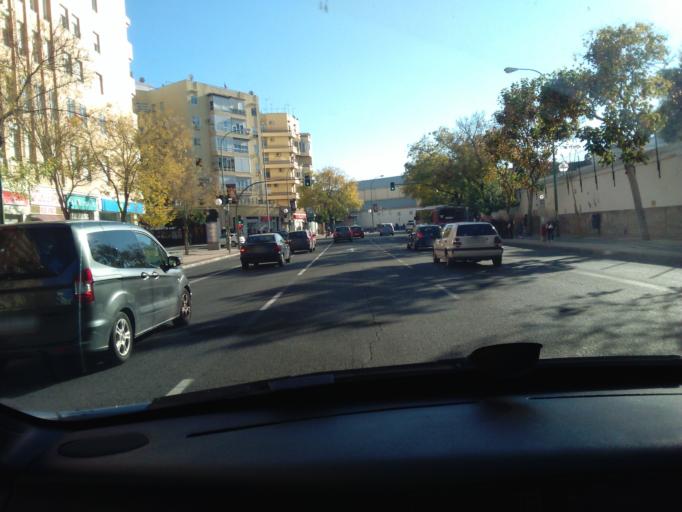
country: ES
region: Andalusia
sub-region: Provincia de Sevilla
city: Sevilla
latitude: 37.3981
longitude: -5.9816
